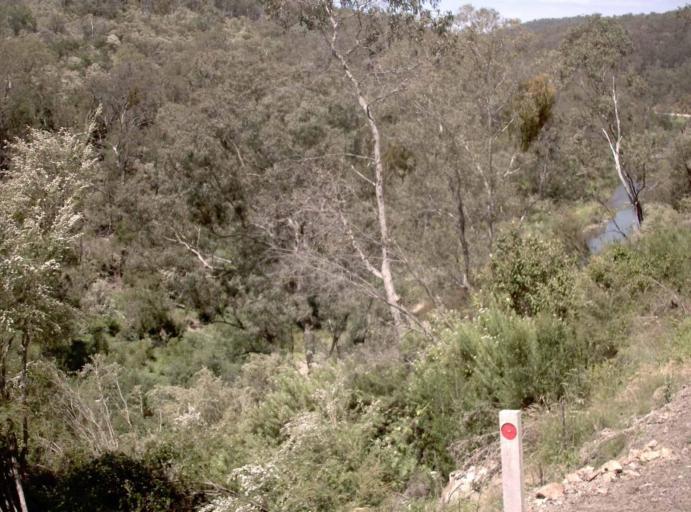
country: AU
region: Victoria
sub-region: East Gippsland
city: Bairnsdale
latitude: -37.4517
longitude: 147.8282
